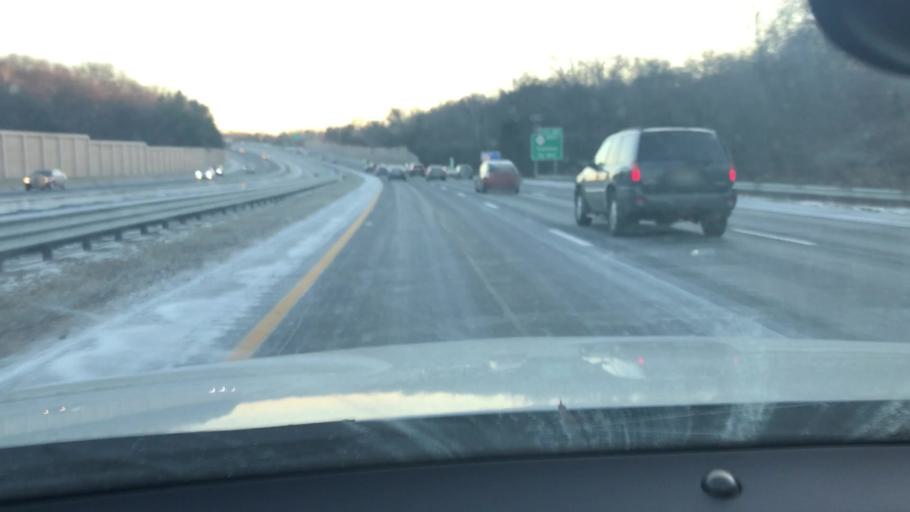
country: US
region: New Jersey
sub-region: Mercer County
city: Mercerville
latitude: 40.2408
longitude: -74.7018
